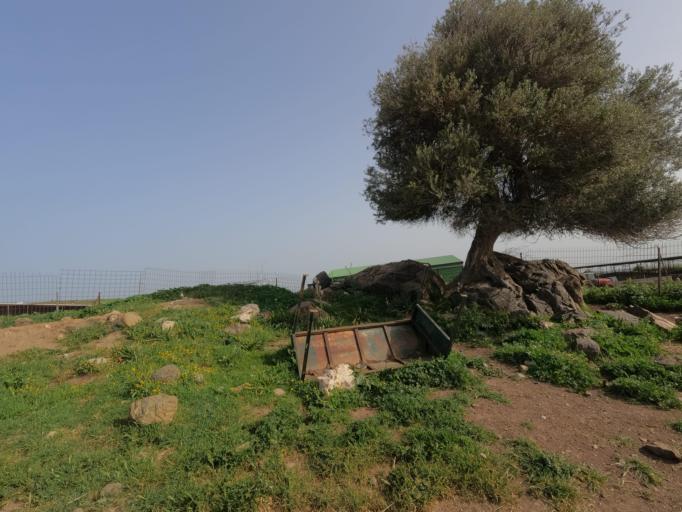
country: CY
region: Pafos
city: Polis
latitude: 34.9956
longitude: 32.3557
